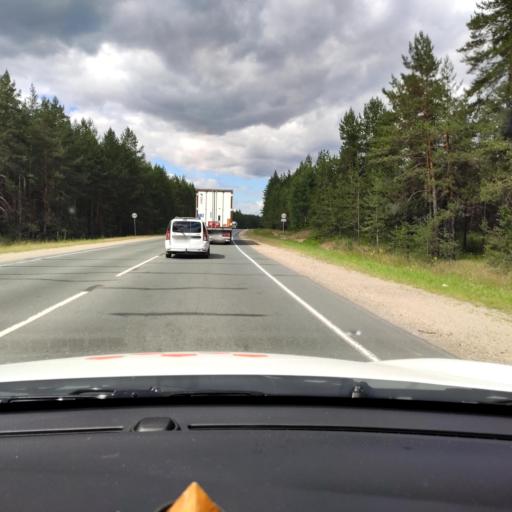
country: RU
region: Mariy-El
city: Krasnogorskiy
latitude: 56.1006
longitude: 48.3439
